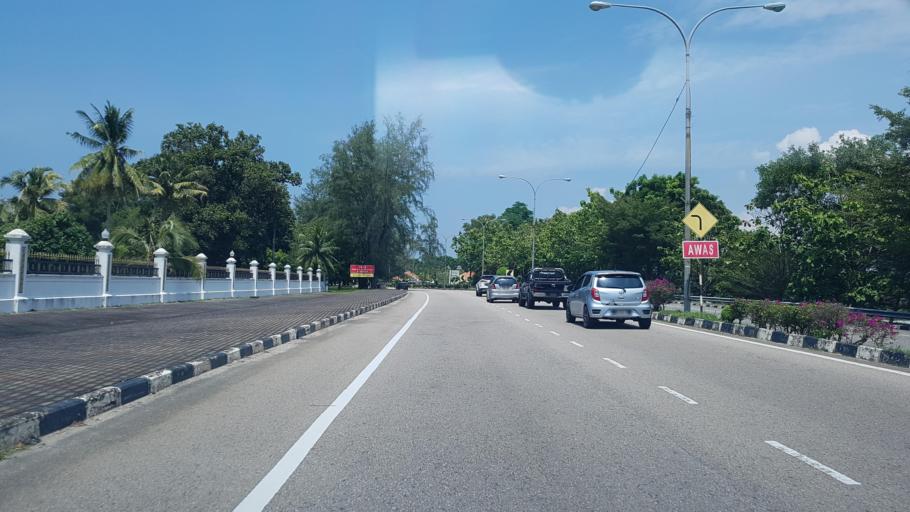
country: MY
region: Terengganu
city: Kuala Terengganu
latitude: 5.3030
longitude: 103.1612
